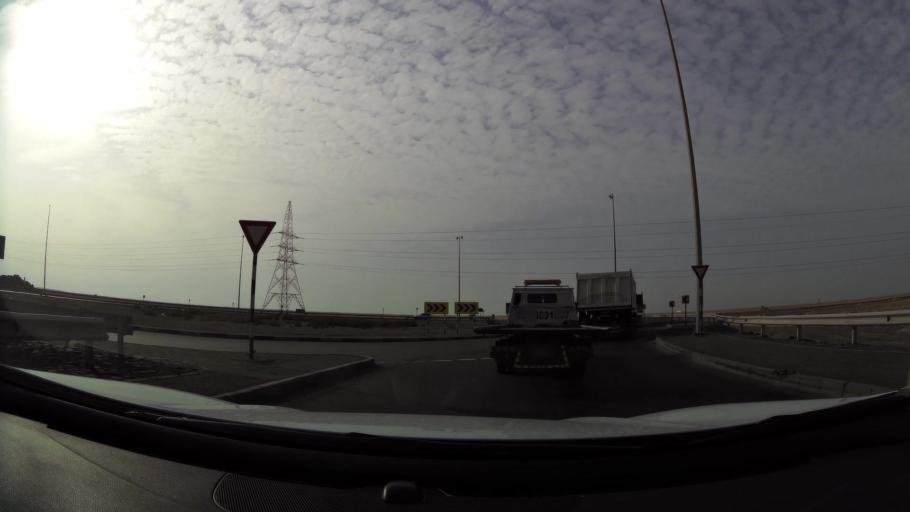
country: AE
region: Abu Dhabi
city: Abu Dhabi
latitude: 24.2175
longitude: 54.4131
